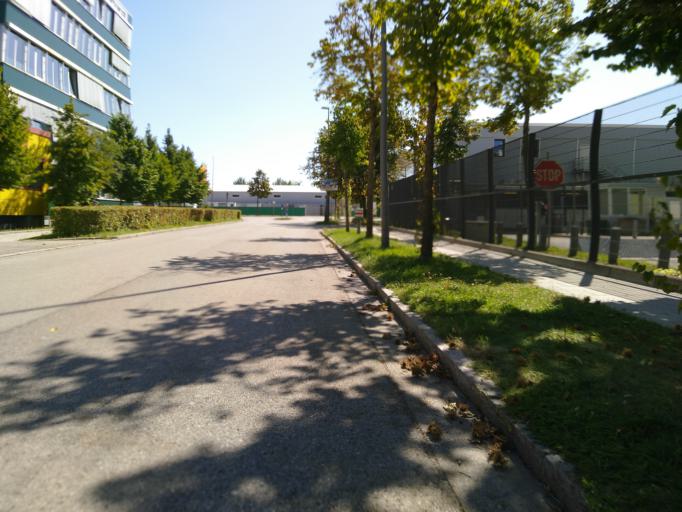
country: DE
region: Bavaria
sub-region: Upper Bavaria
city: Bogenhausen
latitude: 48.1936
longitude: 11.5933
